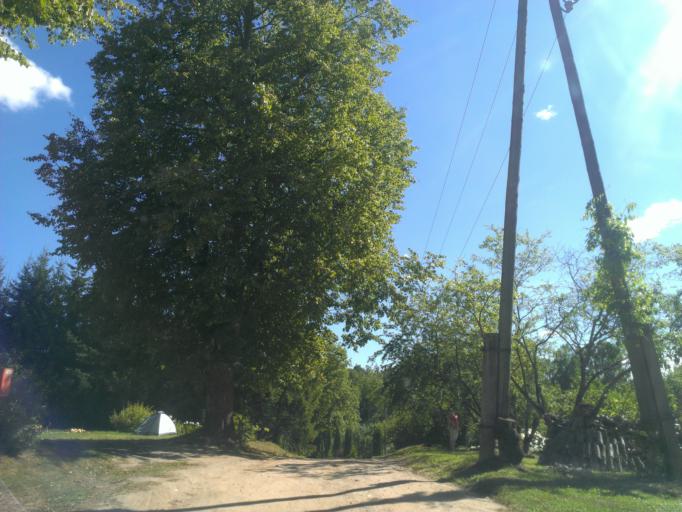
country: LV
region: Malpils
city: Malpils
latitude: 57.0103
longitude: 24.9671
